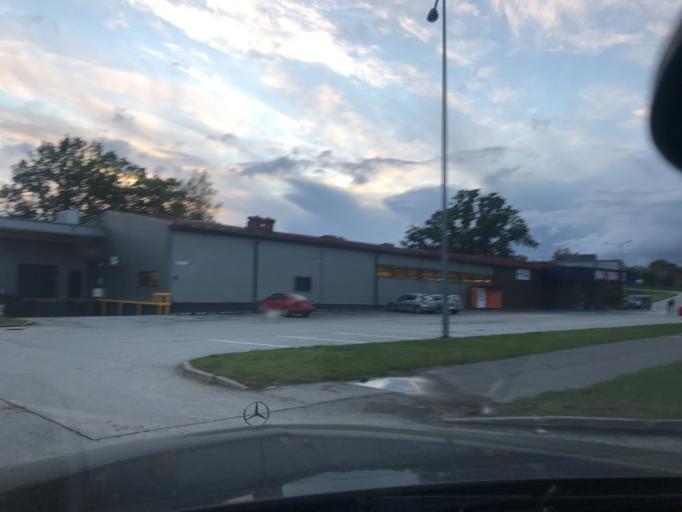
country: EE
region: Valgamaa
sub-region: Torva linn
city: Torva
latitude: 57.9977
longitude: 25.9337
